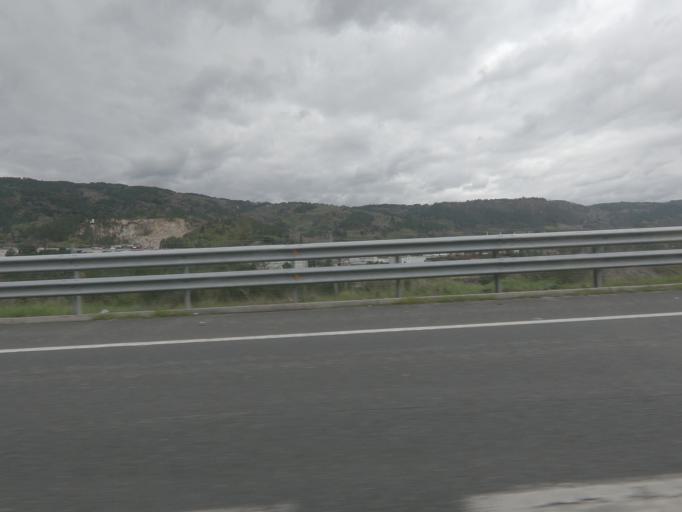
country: ES
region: Galicia
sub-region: Provincia de Ourense
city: Toen
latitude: 42.3461
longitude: -7.9151
